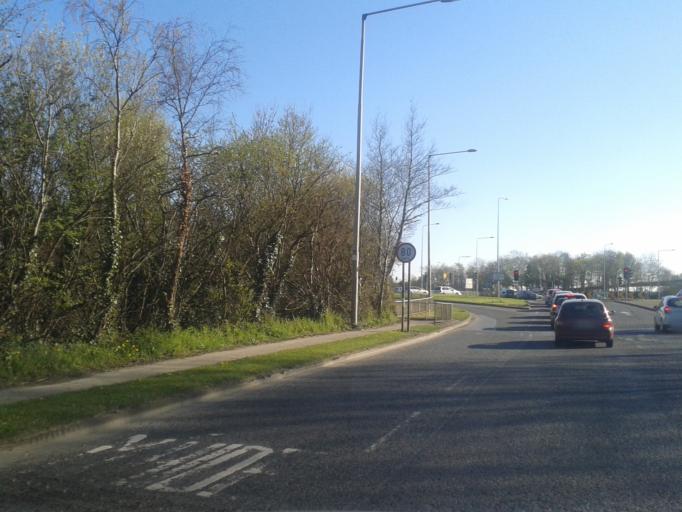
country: IE
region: Leinster
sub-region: Fingal County
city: Swords
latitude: 53.4549
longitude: -6.2133
